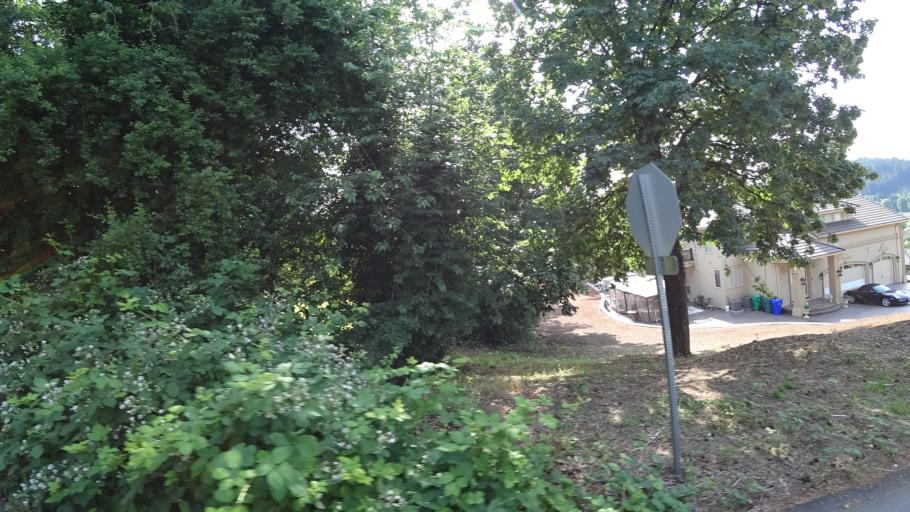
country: US
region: Oregon
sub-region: Clackamas County
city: Happy Valley
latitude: 45.4572
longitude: -122.5205
